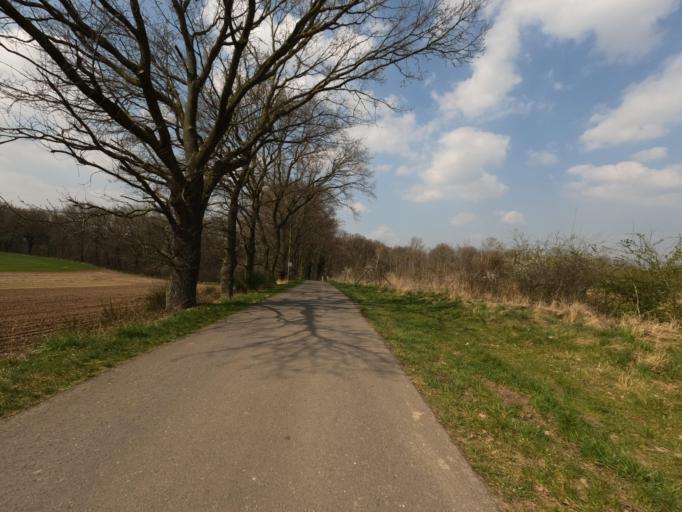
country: DE
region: North Rhine-Westphalia
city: Huckelhoven
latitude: 51.0742
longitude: 6.2337
